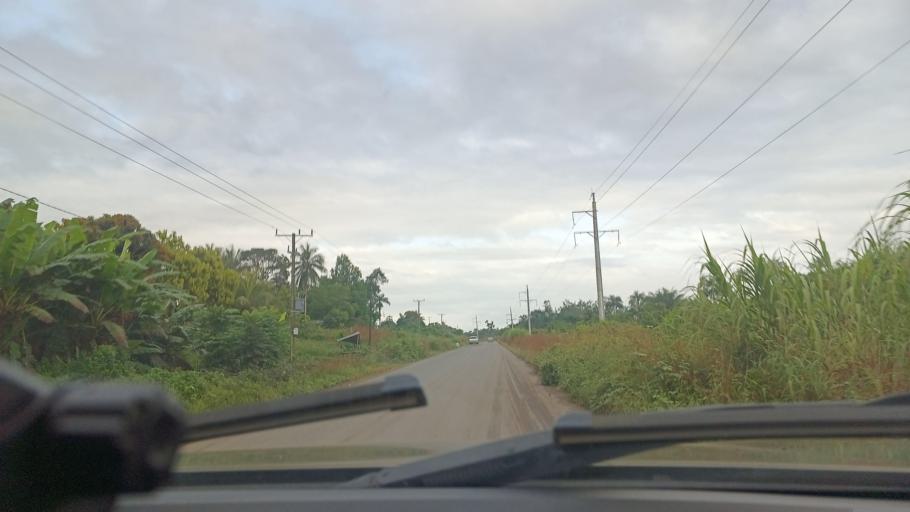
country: LR
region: Montserrado
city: Monrovia
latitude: 6.5638
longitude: -10.8727
